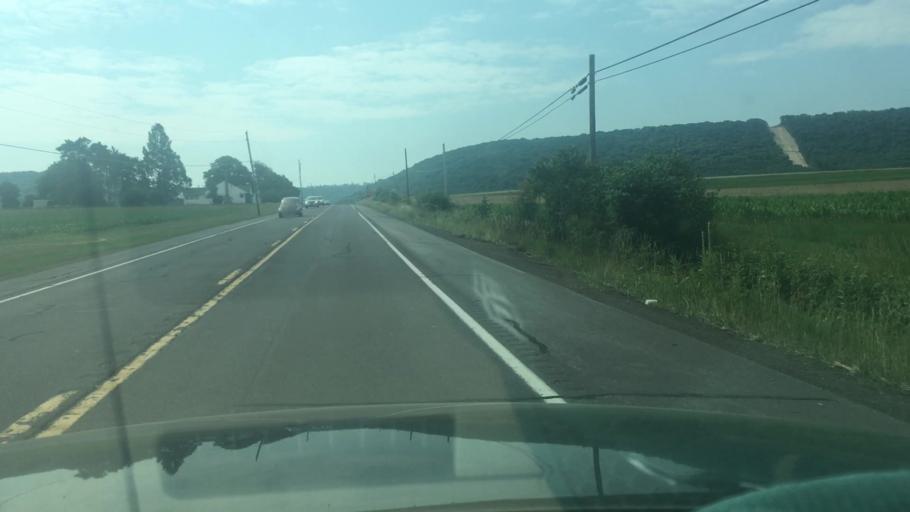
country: US
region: Pennsylvania
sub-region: Northumberland County
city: Elysburg
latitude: 40.8414
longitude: -76.5173
